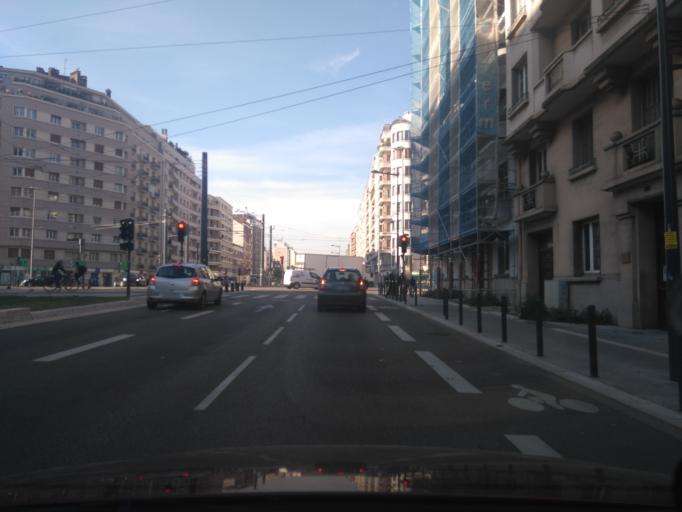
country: FR
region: Rhone-Alpes
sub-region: Departement de l'Isere
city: Grenoble
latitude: 45.1810
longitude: 5.7165
